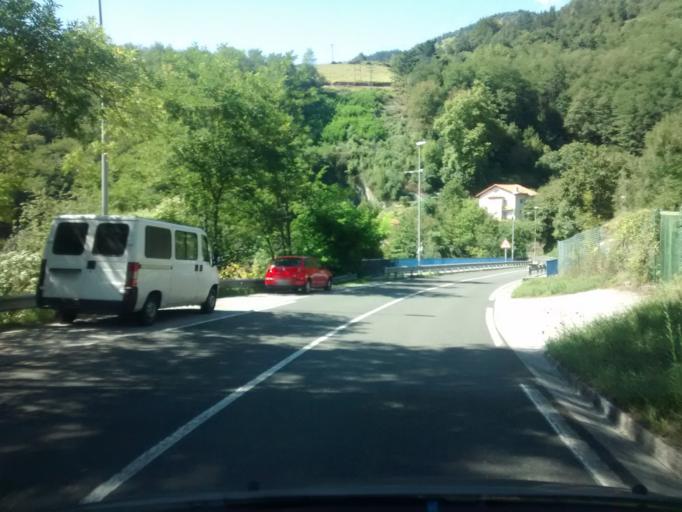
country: ES
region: Basque Country
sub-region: Provincia de Guipuzcoa
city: Eibar
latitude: 43.1876
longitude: -2.4715
